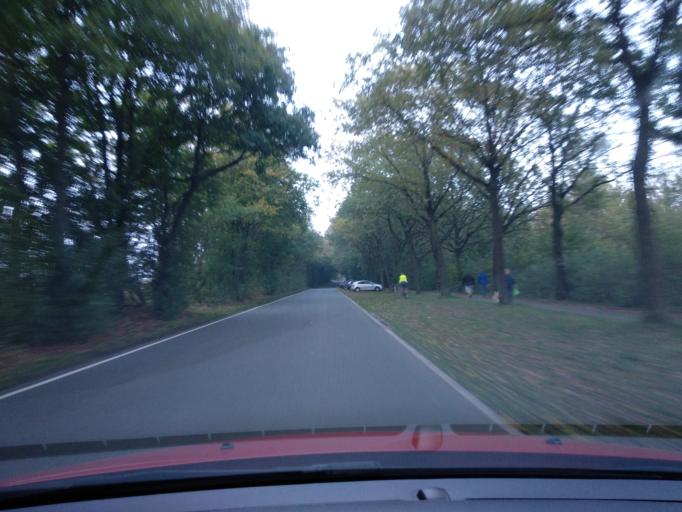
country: DE
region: North Rhine-Westphalia
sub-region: Regierungsbezirk Detmold
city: Paderborn
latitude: 51.6869
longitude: 8.7814
